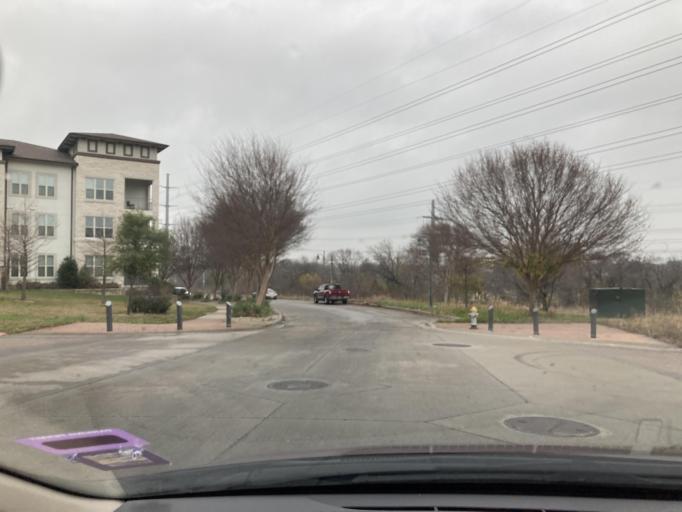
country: US
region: Texas
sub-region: Dallas County
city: University Park
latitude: 32.8952
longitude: -96.7660
